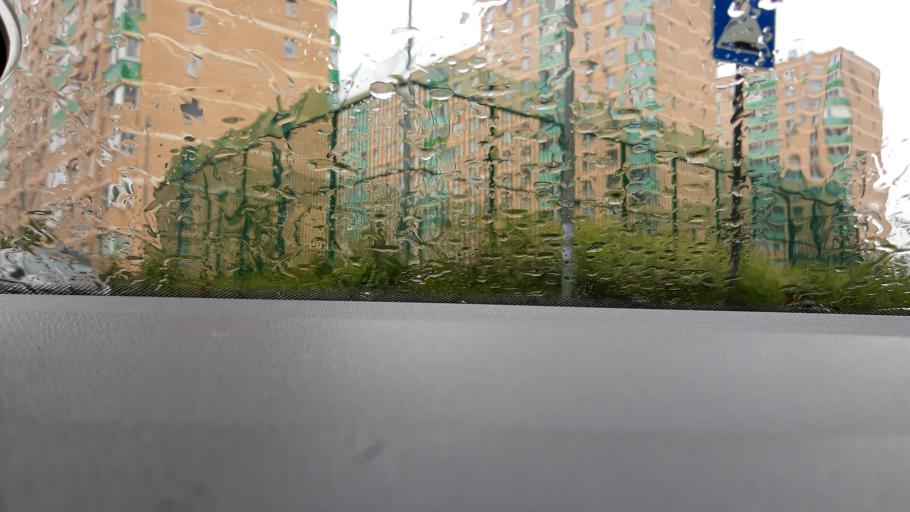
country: RU
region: Moskovskaya
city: Kommunarka
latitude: 55.5751
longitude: 37.4750
